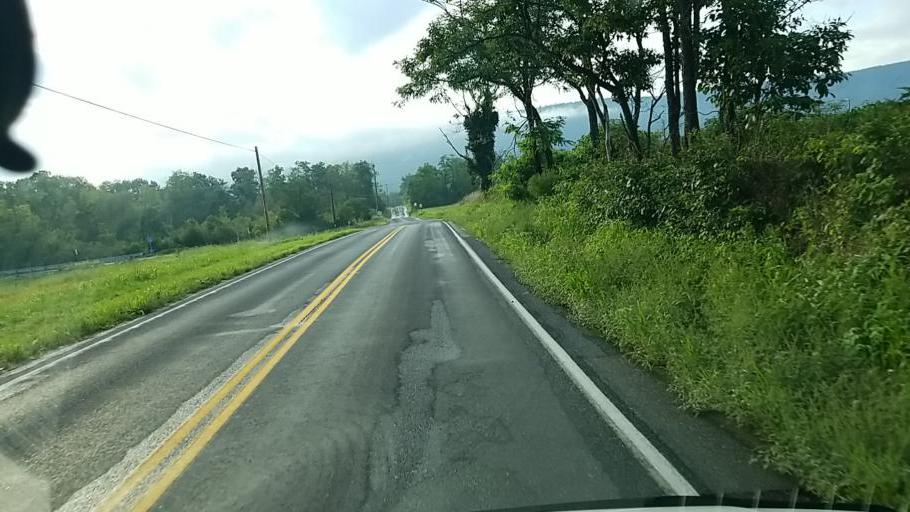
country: US
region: Pennsylvania
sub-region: Cumberland County
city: Newville
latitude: 40.1968
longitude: -77.5003
